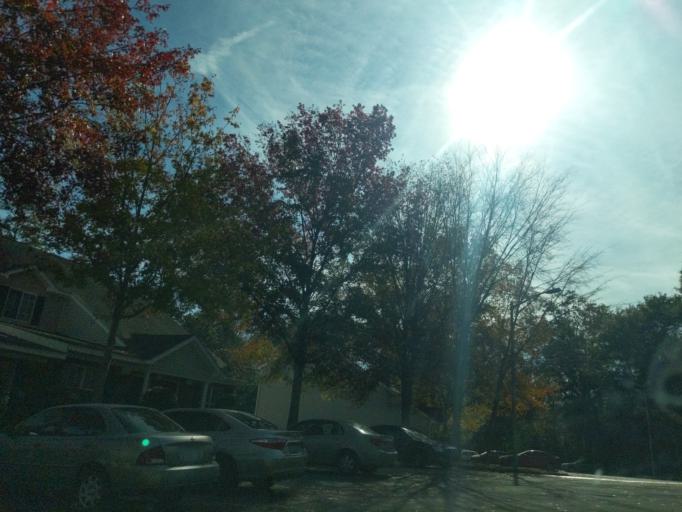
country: US
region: Florida
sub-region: Leon County
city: Tallahassee
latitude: 30.4669
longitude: -84.3403
